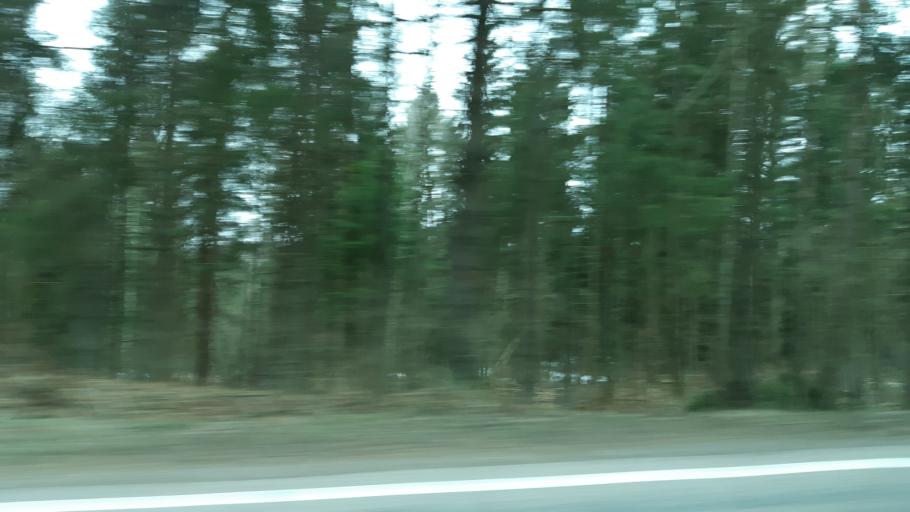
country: PL
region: Podlasie
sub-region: Suwalki
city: Suwalki
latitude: 54.2998
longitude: 22.9566
